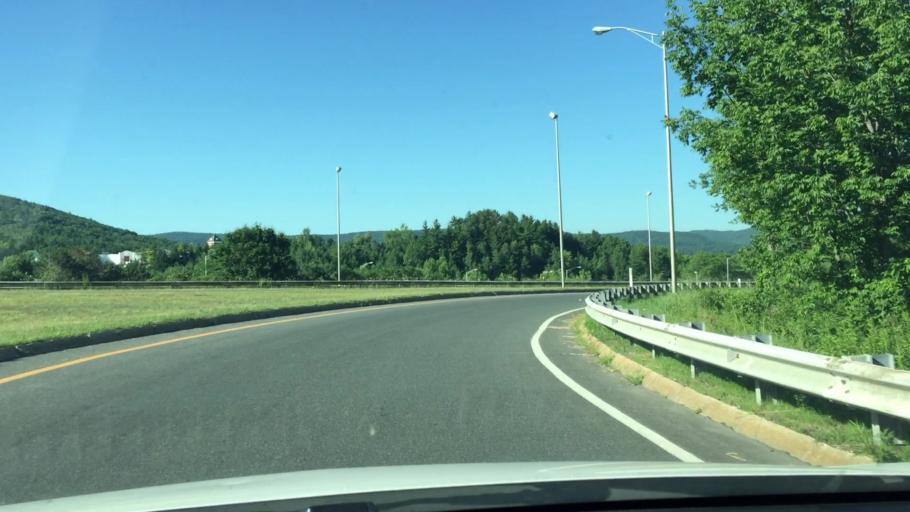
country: US
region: Massachusetts
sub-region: Berkshire County
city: Lee
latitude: 42.2993
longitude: -73.2336
